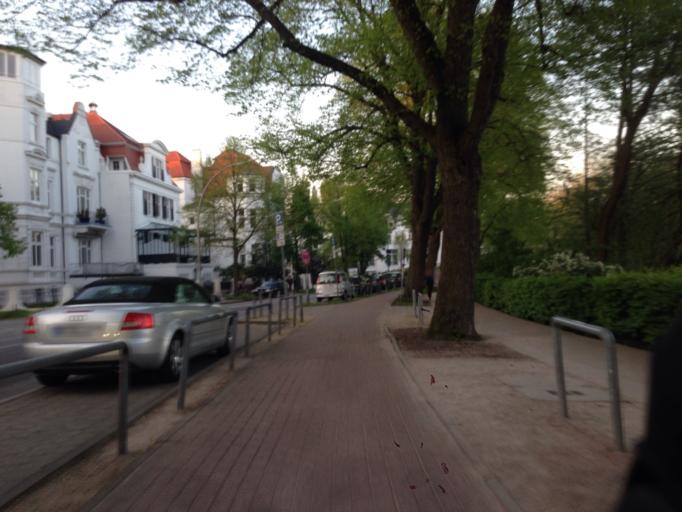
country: DE
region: Hamburg
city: Hamburg
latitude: 53.5806
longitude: 10.0001
